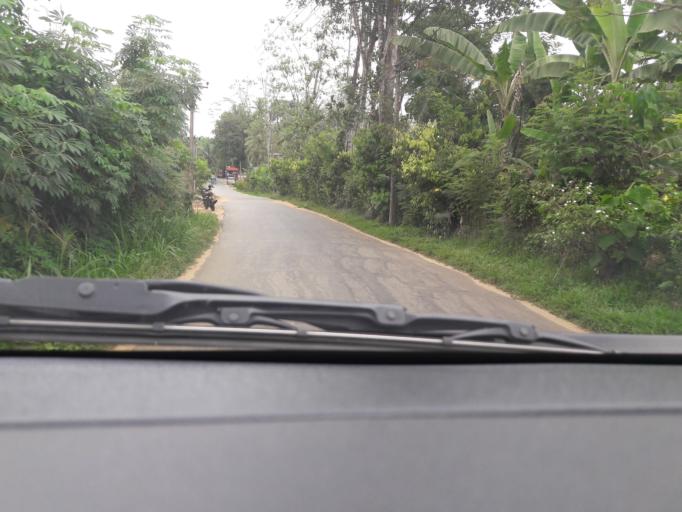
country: LK
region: Southern
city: Hikkaduwa
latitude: 6.2542
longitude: 80.2663
